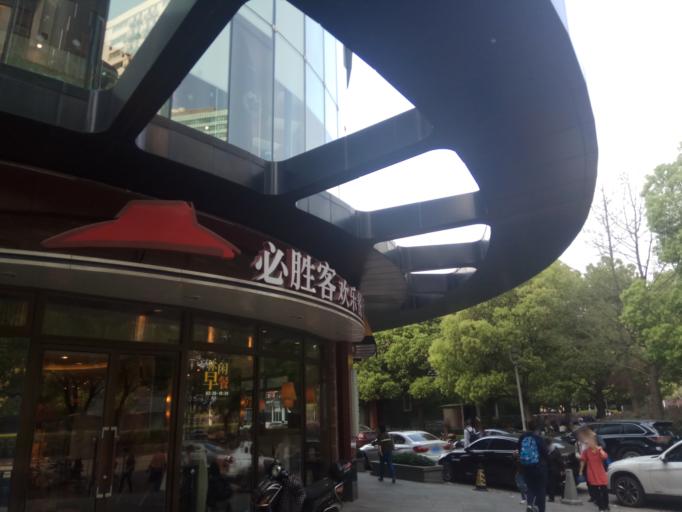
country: CN
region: Shanghai Shi
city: Changning
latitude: 31.2206
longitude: 121.4147
